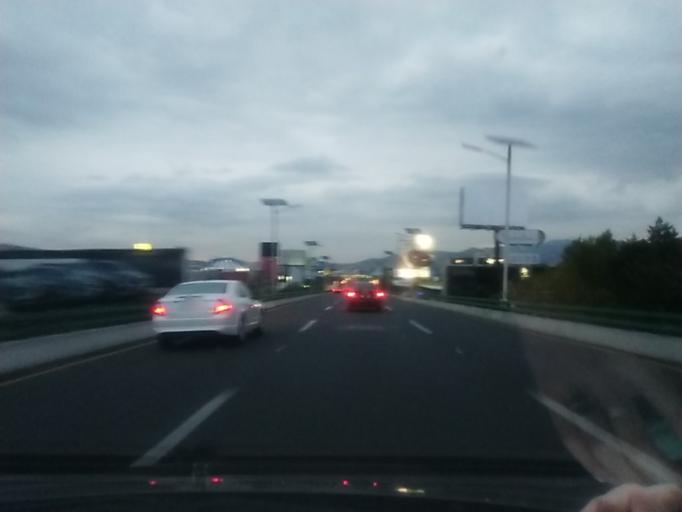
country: MX
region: Mexico
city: Vista Hermosa
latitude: 19.5214
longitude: -99.2284
